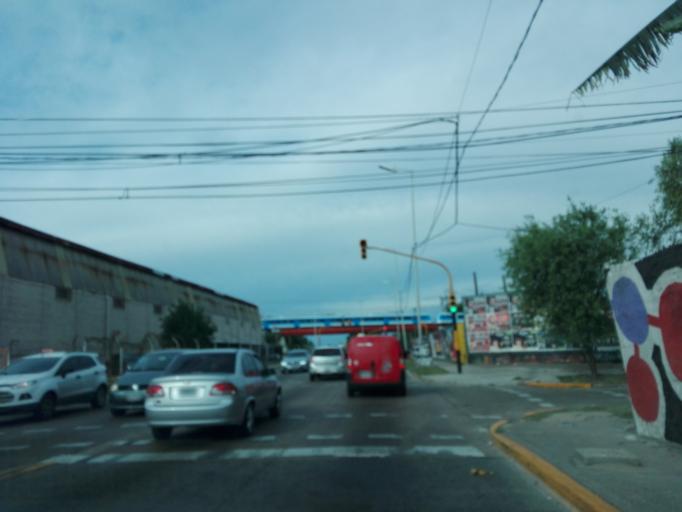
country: AR
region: Buenos Aires
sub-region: Partido de Avellaneda
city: Avellaneda
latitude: -34.6812
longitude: -58.3417
